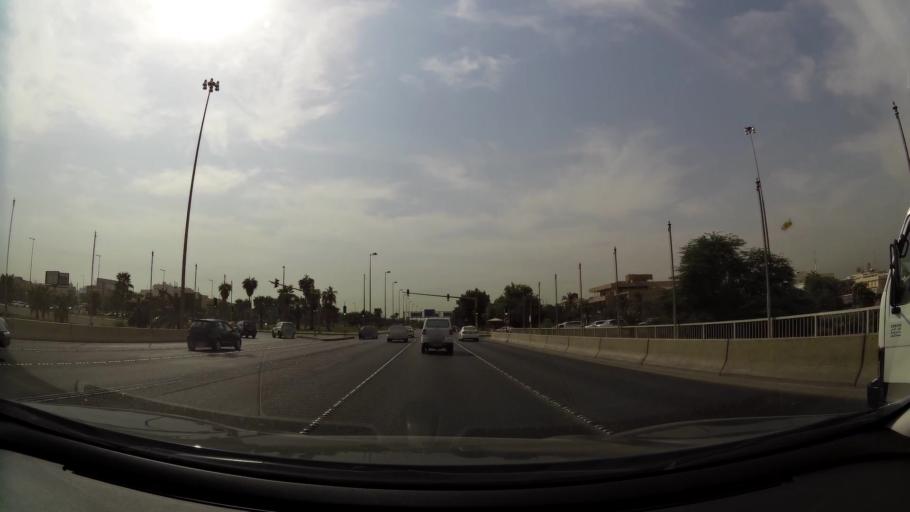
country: KW
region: Al Asimah
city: Kuwait City
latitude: 29.3589
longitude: 47.9736
